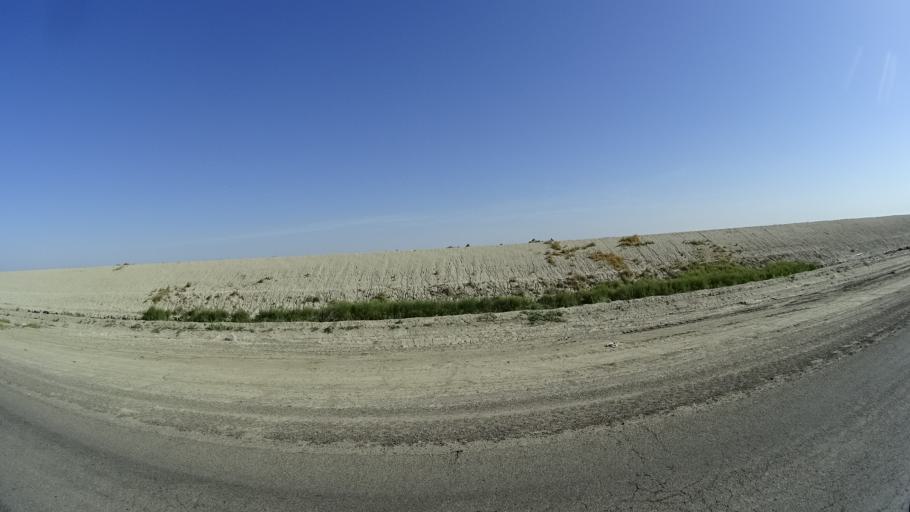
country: US
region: California
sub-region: Kings County
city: Corcoran
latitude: 36.1379
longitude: -119.5607
